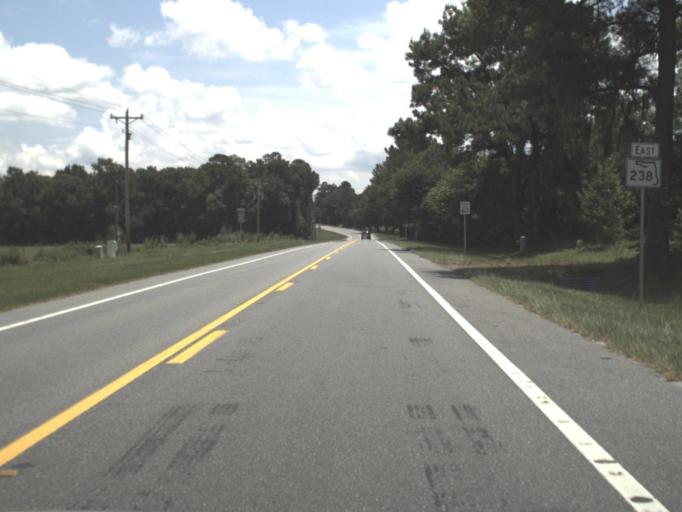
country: US
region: Florida
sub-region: Union County
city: Lake Butler
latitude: 30.0022
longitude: -82.5097
